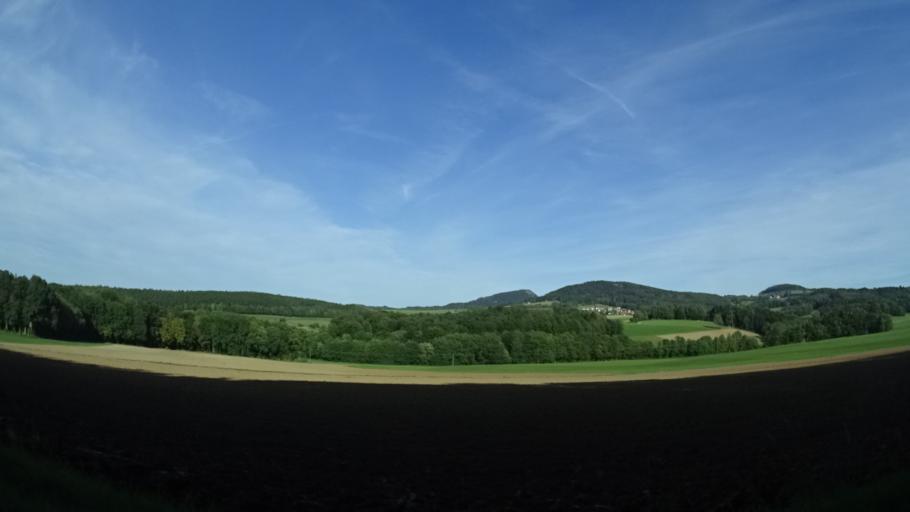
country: DE
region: Hesse
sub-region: Regierungsbezirk Kassel
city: Dipperz
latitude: 50.5379
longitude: 9.8328
